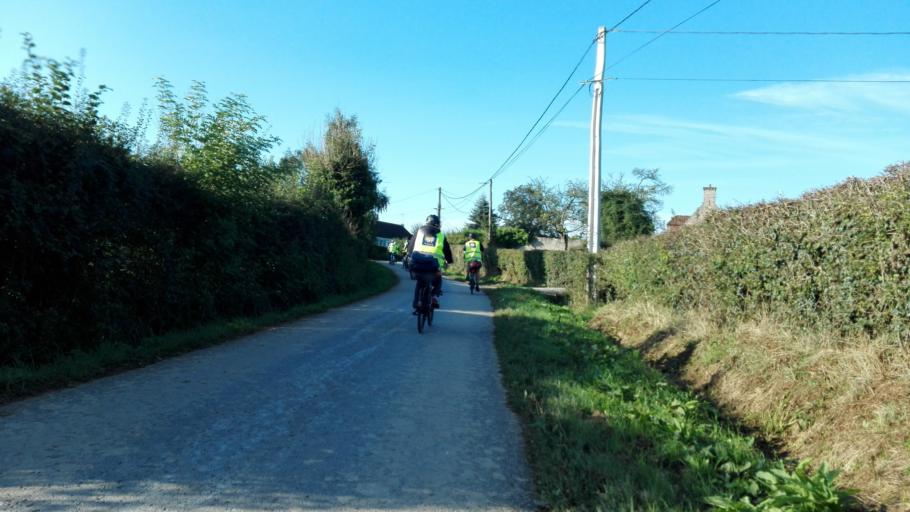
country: FR
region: Nord-Pas-de-Calais
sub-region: Departement du Pas-de-Calais
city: Eperlecques
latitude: 50.8208
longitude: 2.1634
